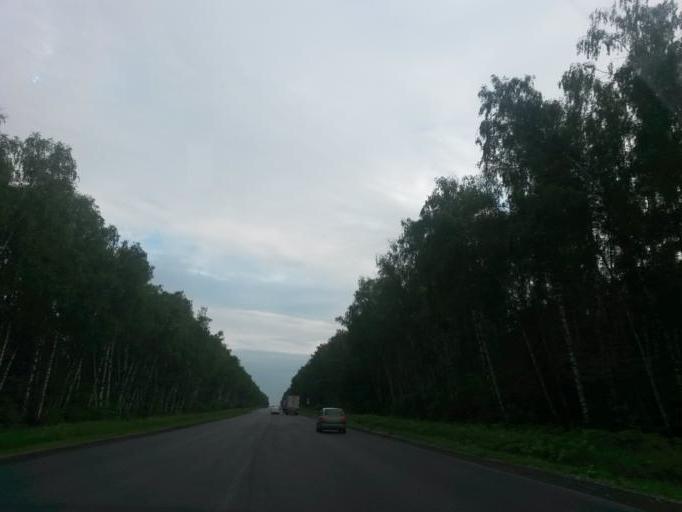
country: RU
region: Moskovskaya
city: Belyye Stolby
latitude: 55.2890
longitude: 37.8207
